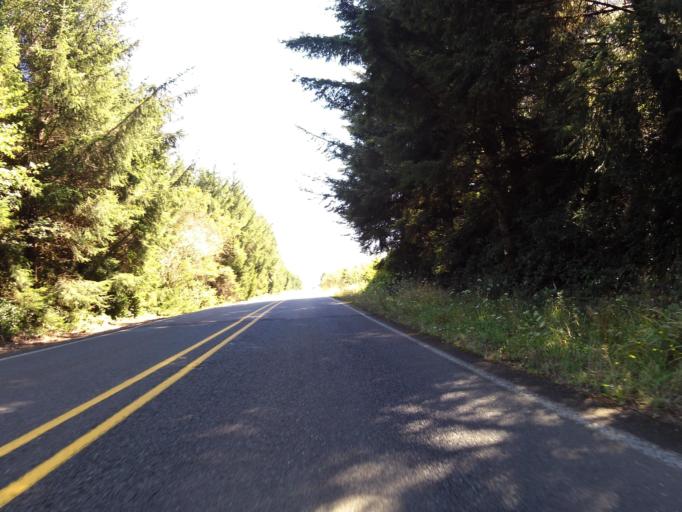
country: US
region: Oregon
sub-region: Coos County
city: Barview
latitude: 43.2625
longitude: -124.3425
